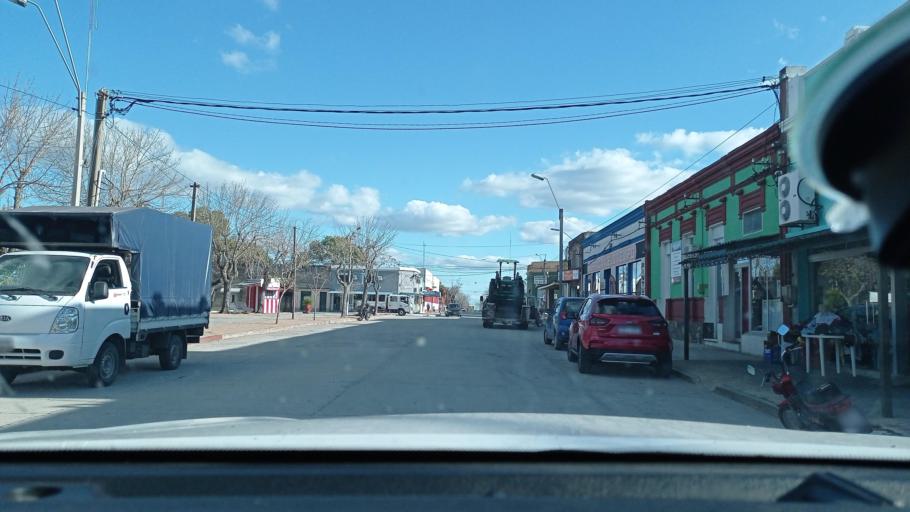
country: UY
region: Florida
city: Casupa
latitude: -34.1002
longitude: -55.6516
